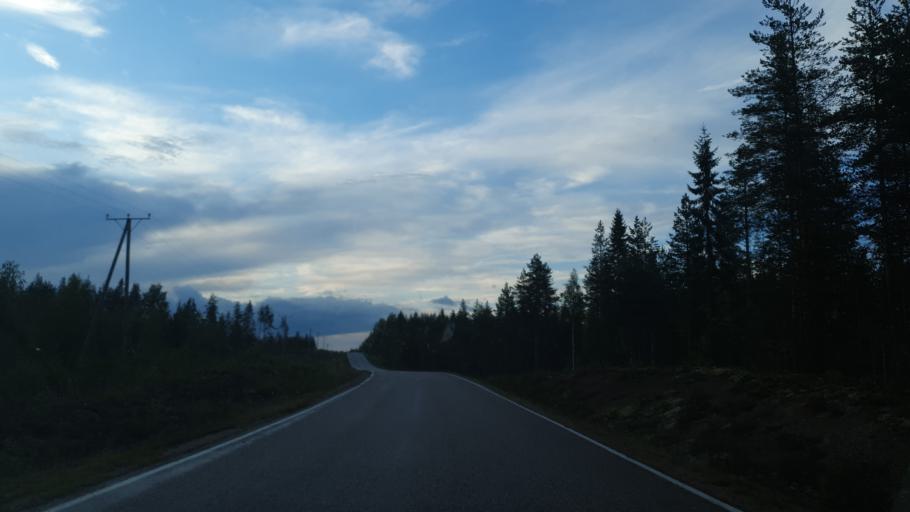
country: FI
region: Kainuu
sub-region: Kehys-Kainuu
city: Kuhmo
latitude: 63.8361
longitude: 29.8437
